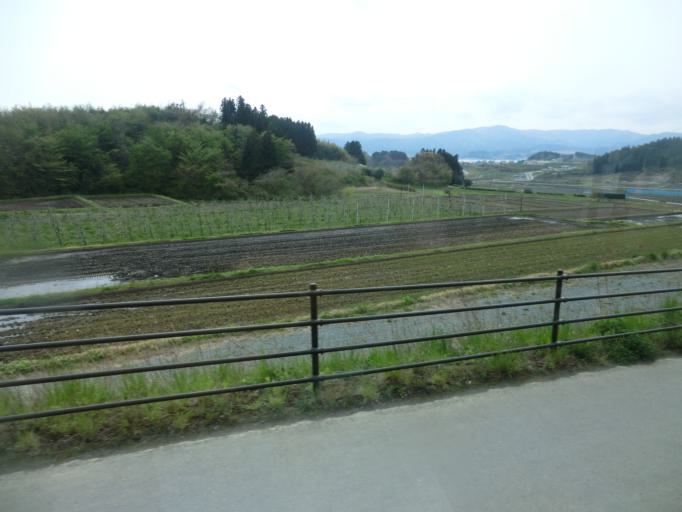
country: JP
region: Iwate
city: Ofunato
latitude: 39.0099
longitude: 141.6760
